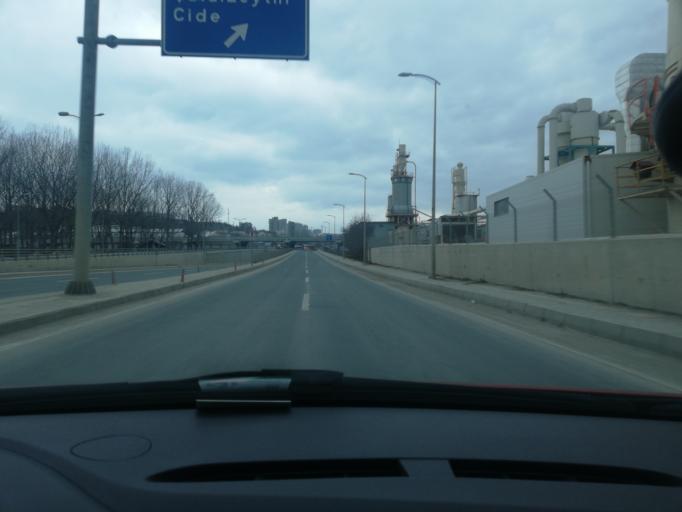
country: TR
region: Kastamonu
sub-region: Cide
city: Kastamonu
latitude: 41.4146
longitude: 33.8001
